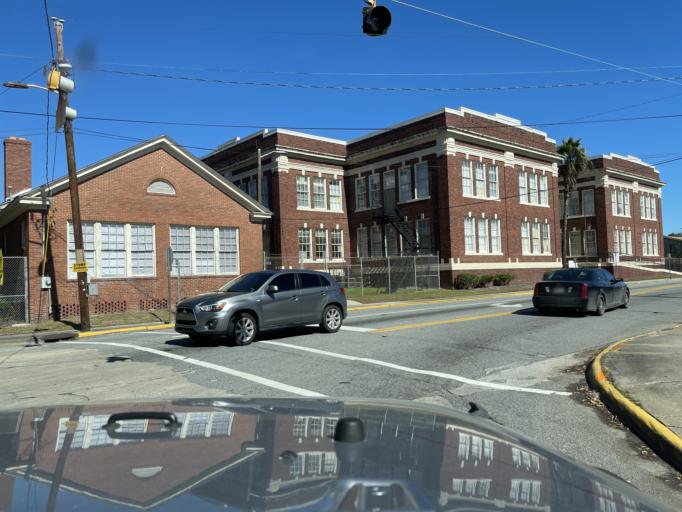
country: US
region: Georgia
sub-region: Chatham County
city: Savannah
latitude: 32.0644
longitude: -81.1058
